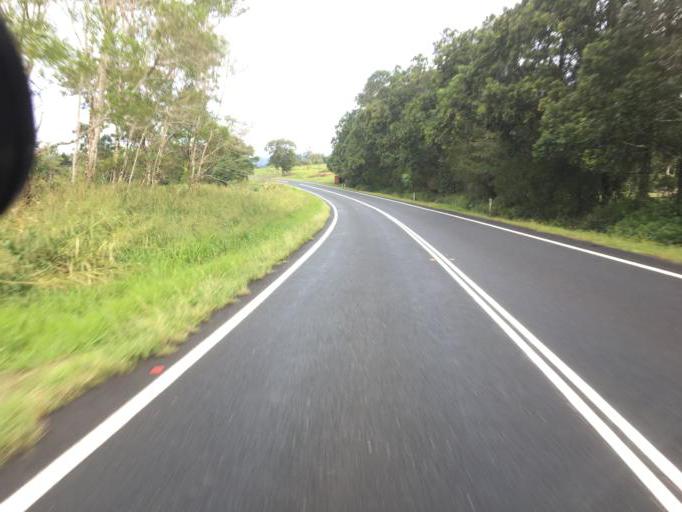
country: AU
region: Queensland
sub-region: Tablelands
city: Ravenshoe
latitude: -17.5252
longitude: 145.6457
